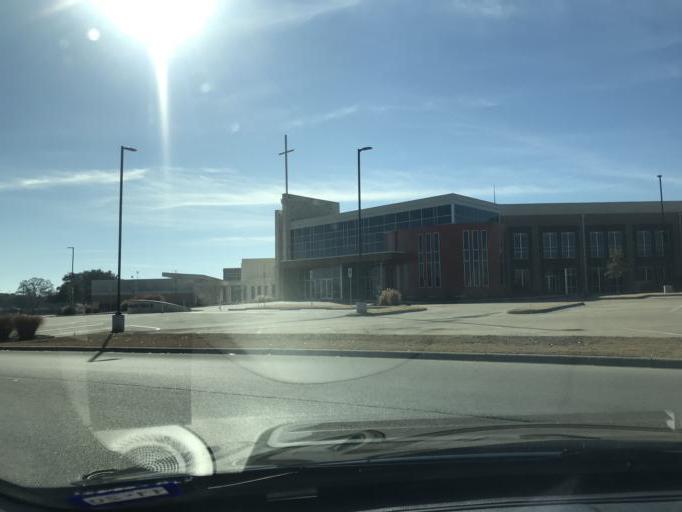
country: US
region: Texas
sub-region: Denton County
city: Denton
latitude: 33.2263
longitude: -97.1487
